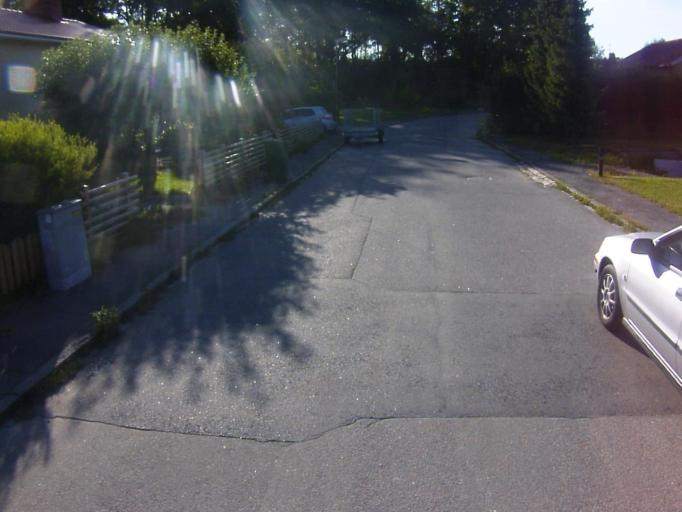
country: SE
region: Soedermanland
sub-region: Eskilstuna Kommun
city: Eskilstuna
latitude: 59.3824
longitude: 16.5364
